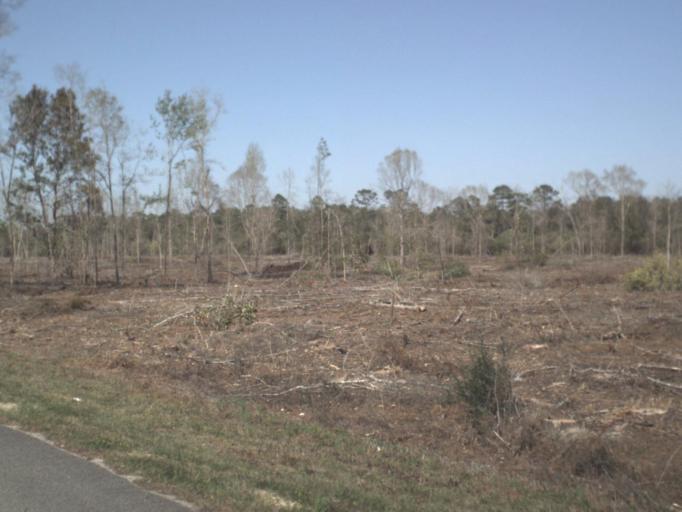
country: US
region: Florida
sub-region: Gulf County
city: Wewahitchka
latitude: 30.1600
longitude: -85.2093
